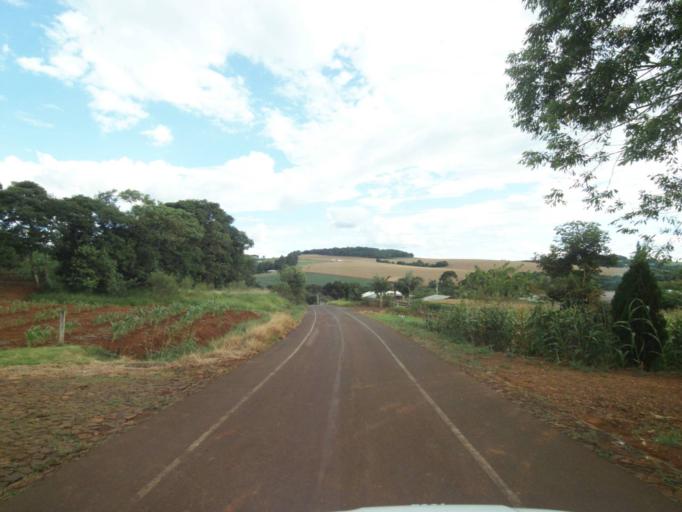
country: BR
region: Parana
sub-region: Laranjeiras Do Sul
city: Laranjeiras do Sul
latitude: -25.4972
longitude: -52.5267
